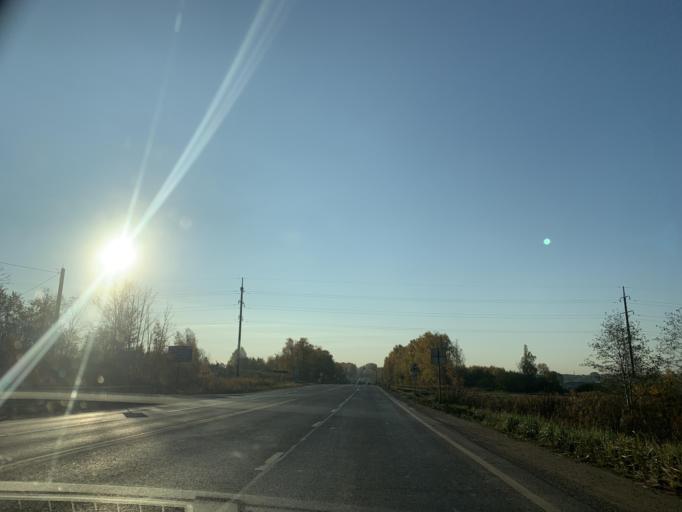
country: RU
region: Jaroslavl
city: Konstantinovskiy
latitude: 57.7348
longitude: 39.7347
